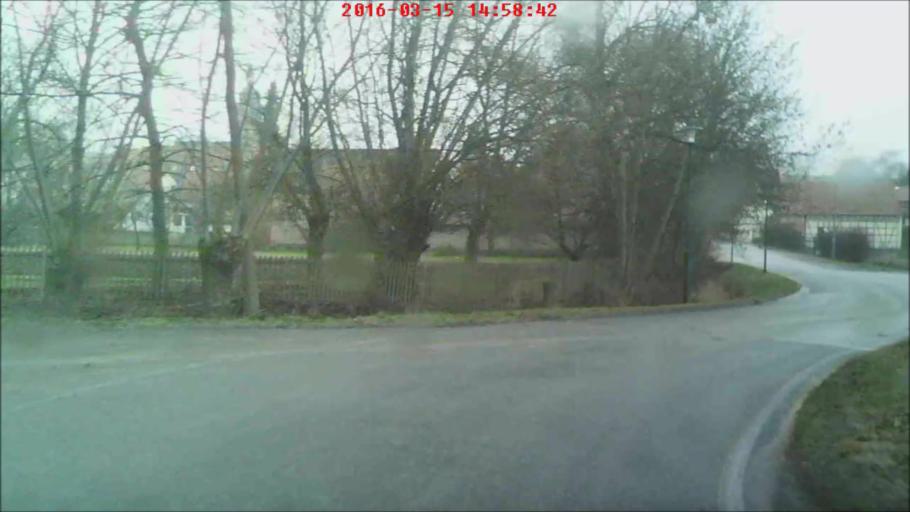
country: DE
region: Thuringia
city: Rockhausen
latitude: 50.9042
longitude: 11.0377
